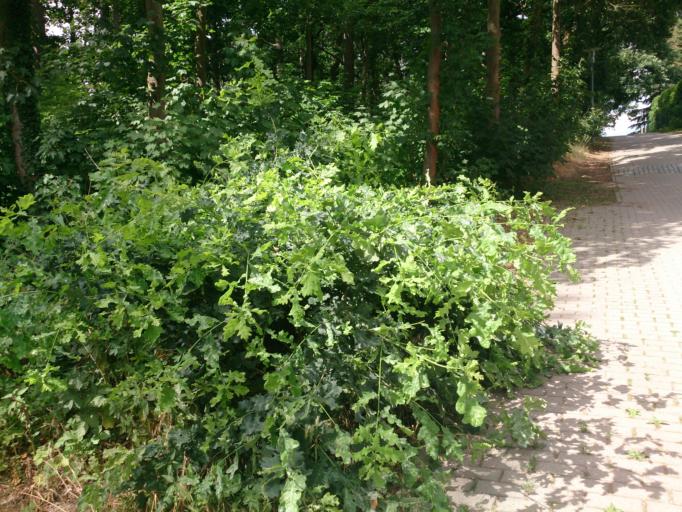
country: DE
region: Mecklenburg-Vorpommern
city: Waren
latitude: 53.5044
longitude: 12.6938
